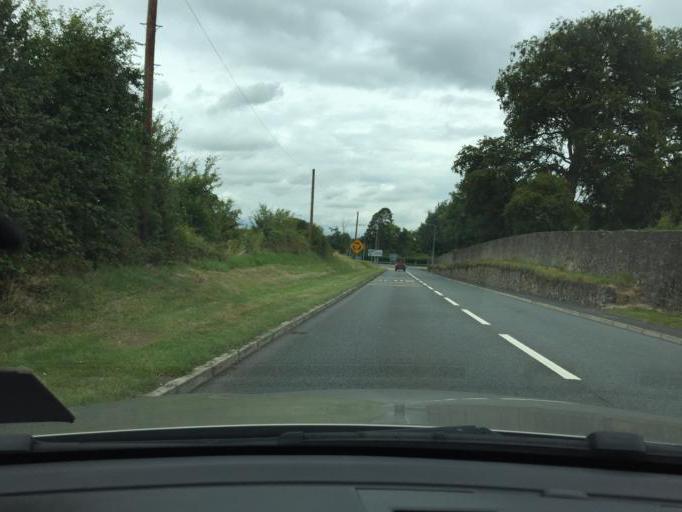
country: IE
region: Leinster
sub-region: Kildare
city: Maynooth
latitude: 53.3868
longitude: -6.5759
